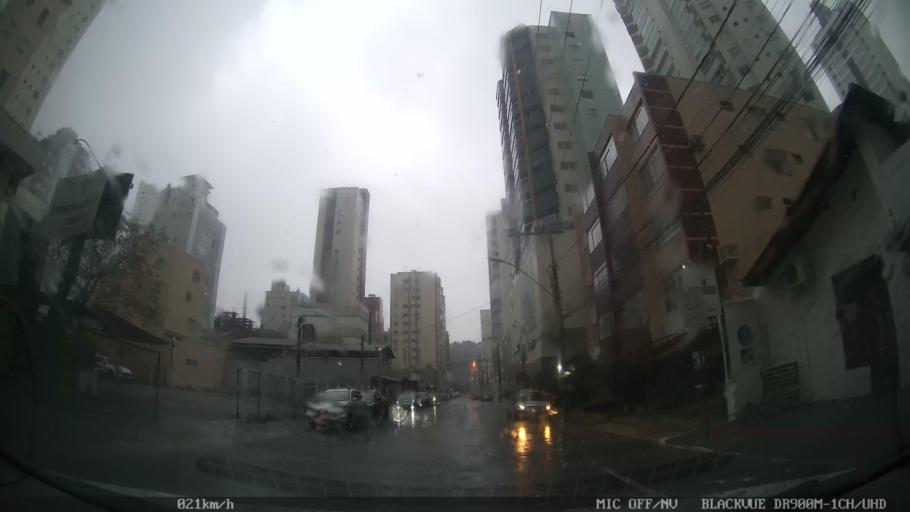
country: BR
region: Santa Catarina
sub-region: Balneario Camboriu
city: Balneario Camboriu
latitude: -26.9728
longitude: -48.6368
